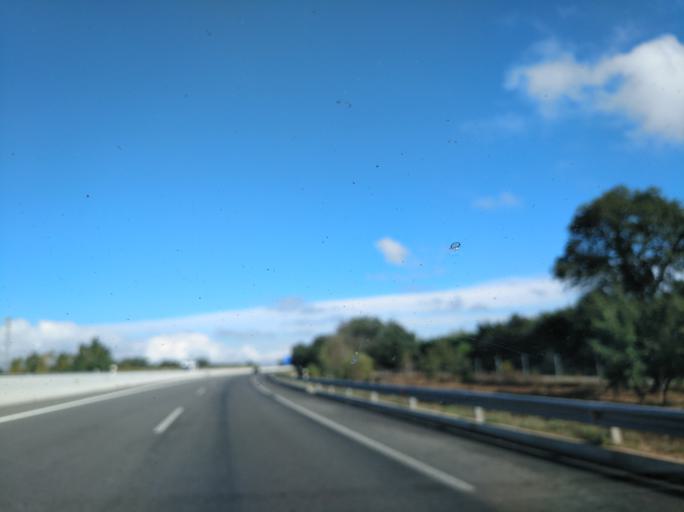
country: ES
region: Catalonia
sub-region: Provincia de Girona
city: Sils
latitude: 41.8203
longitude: 2.7633
